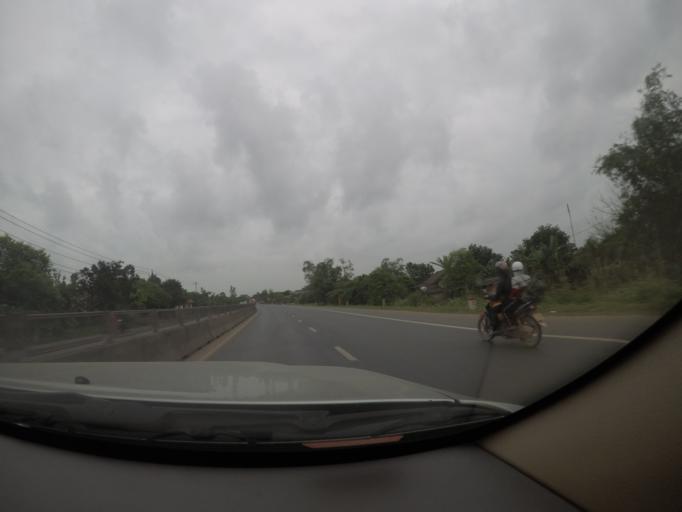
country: VN
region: Quang Tri
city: Hai Lang
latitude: 16.7183
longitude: 107.2098
